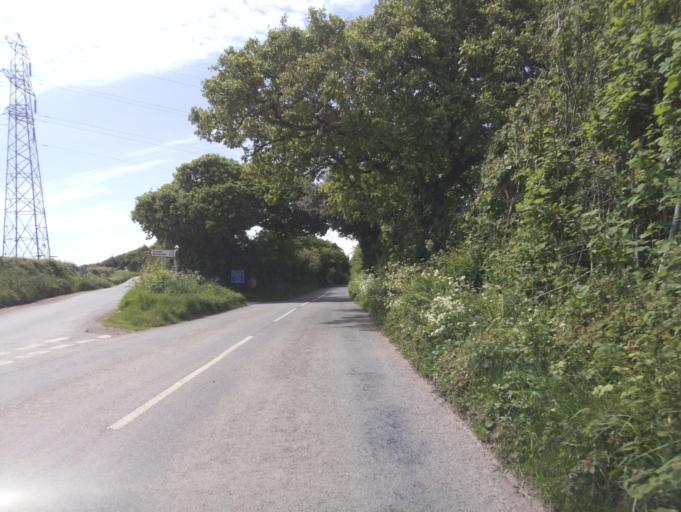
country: GB
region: England
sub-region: Devon
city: Kingsbridge
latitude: 50.3604
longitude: -3.7512
